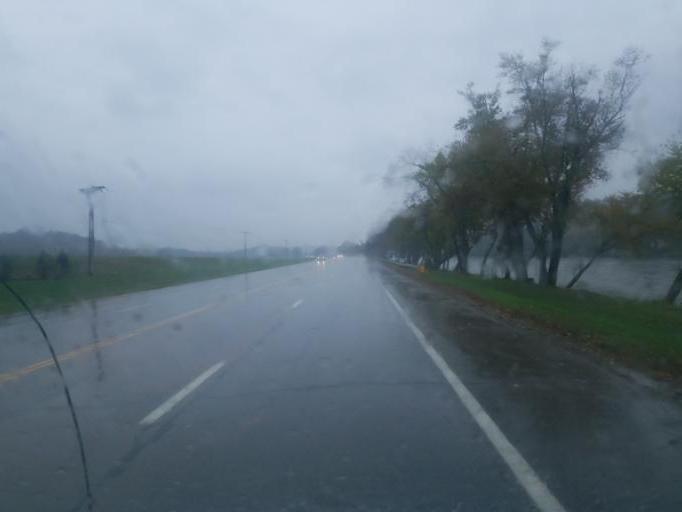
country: US
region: Ohio
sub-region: Muskingum County
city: South Zanesville
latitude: 39.8720
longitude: -81.9494
